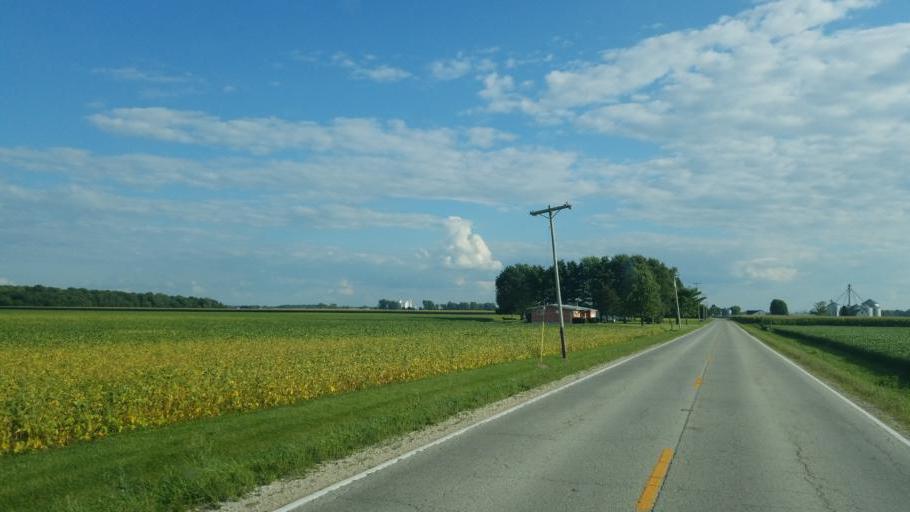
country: US
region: Ohio
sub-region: Sandusky County
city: Ballville
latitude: 41.2617
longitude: -83.1313
